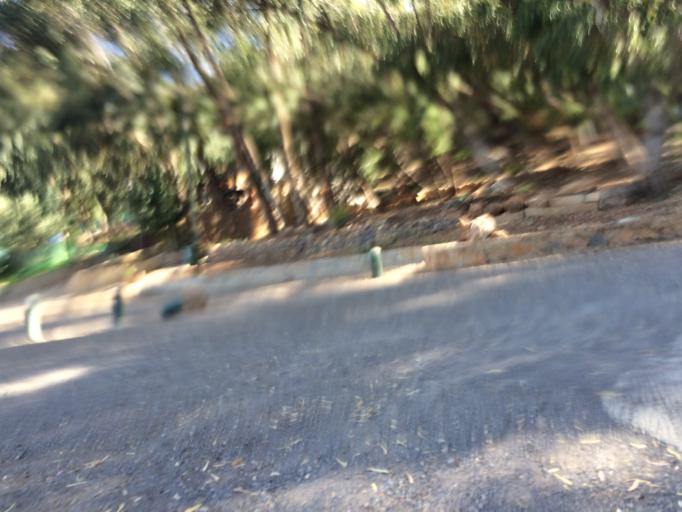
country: MA
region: Tanger-Tetouan
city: Chefchaouene
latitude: 35.1740
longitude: -5.2638
